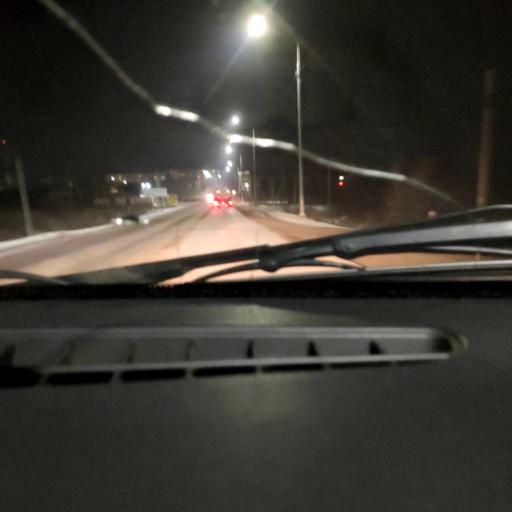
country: RU
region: Bashkortostan
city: Avdon
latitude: 54.6052
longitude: 55.8468
